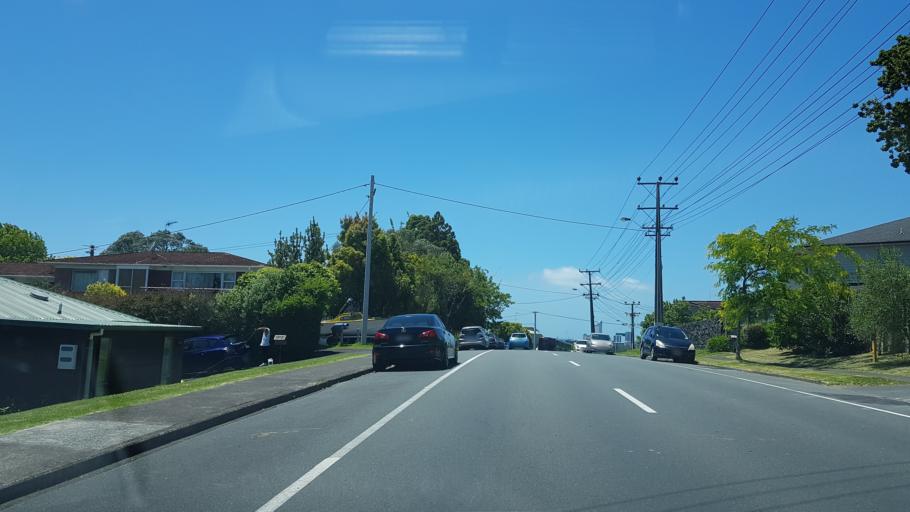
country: NZ
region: Auckland
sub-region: Auckland
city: North Shore
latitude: -36.7804
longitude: 174.7343
